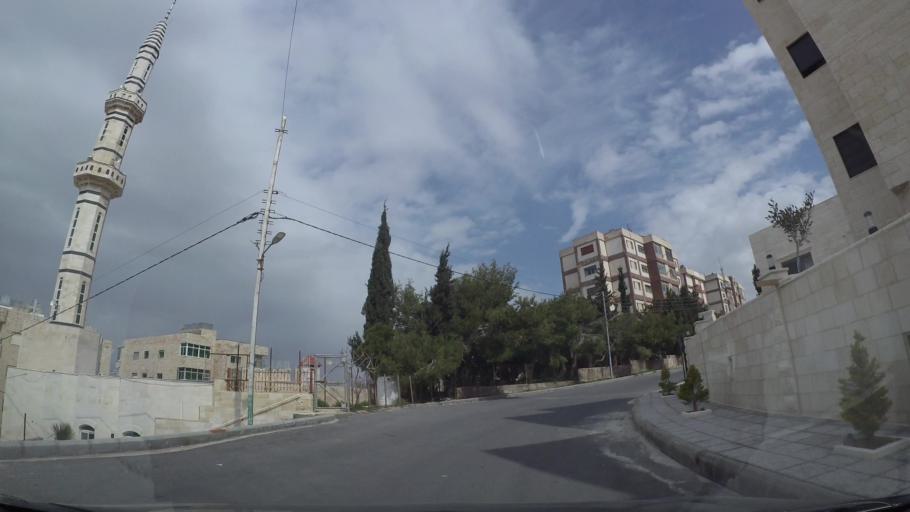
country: JO
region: Amman
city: Amman
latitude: 31.9896
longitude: 35.9203
